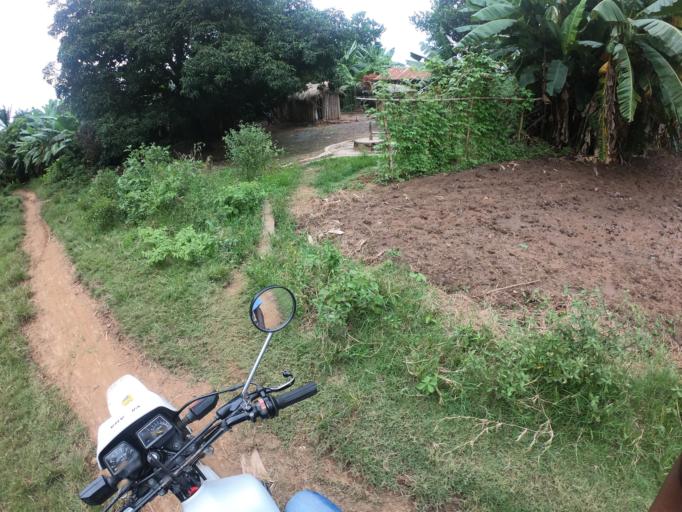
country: TZ
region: Mbeya
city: Kyela
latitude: -9.6614
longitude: 33.8321
